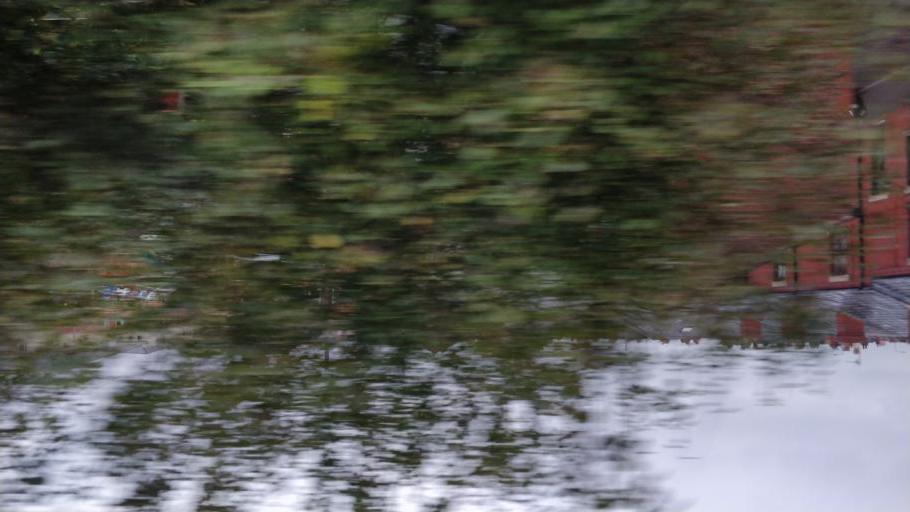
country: GB
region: England
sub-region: Borough of Wigan
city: Ince-in-Makerfield
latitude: 53.5489
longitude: -2.6472
